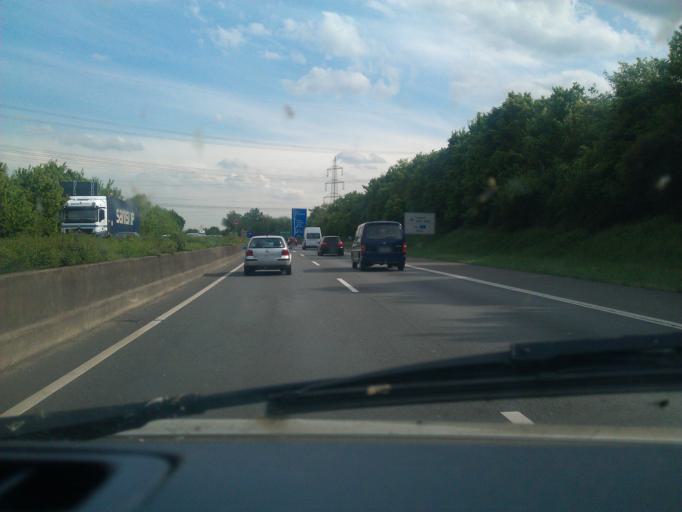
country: DE
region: North Rhine-Westphalia
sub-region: Regierungsbezirk Dusseldorf
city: Moers
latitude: 51.4530
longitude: 6.5927
